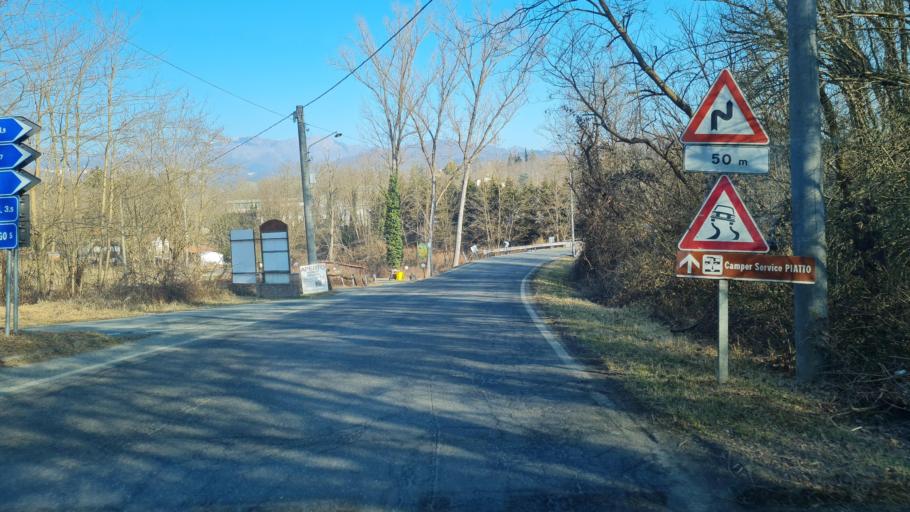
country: IT
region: Piedmont
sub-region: Provincia di Biella
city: Valdengo
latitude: 45.5782
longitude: 8.1378
